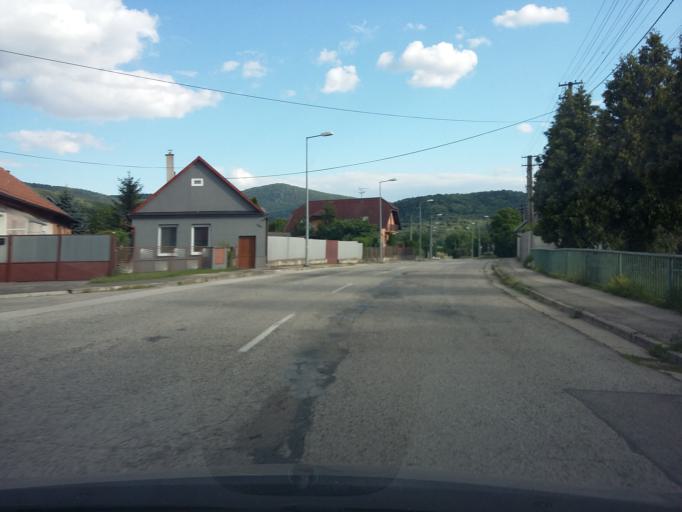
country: SK
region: Trnavsky
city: Smolenice
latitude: 48.5549
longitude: 17.3499
